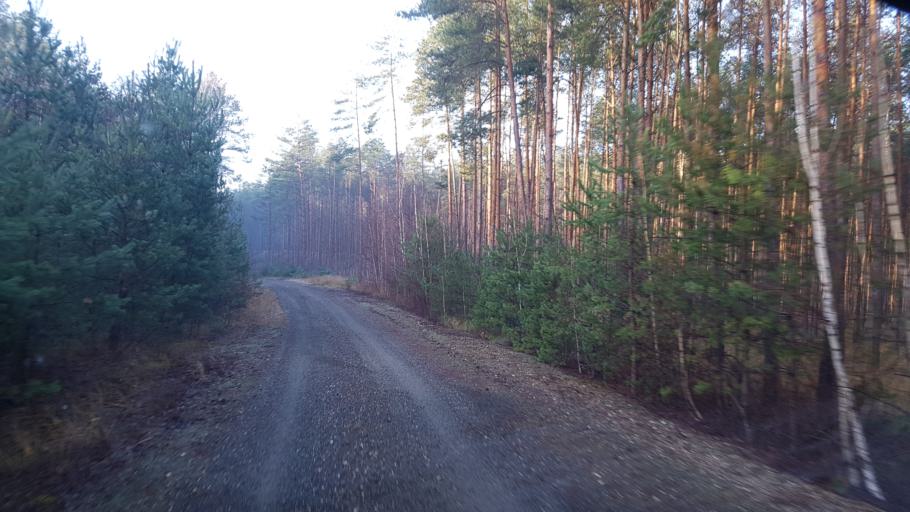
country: DE
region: Brandenburg
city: Schonborn
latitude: 51.5799
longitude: 13.4637
